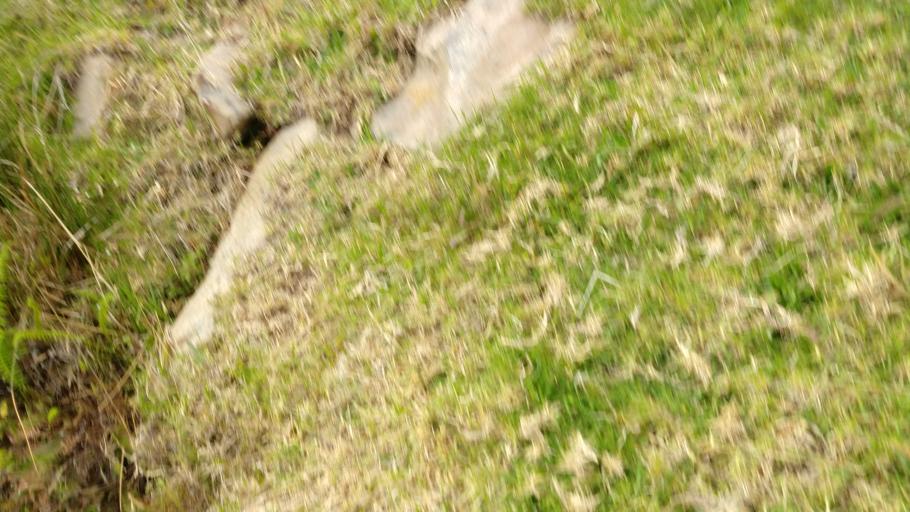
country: CO
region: Boyaca
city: Arcabuco
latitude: 5.7431
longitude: -73.4180
